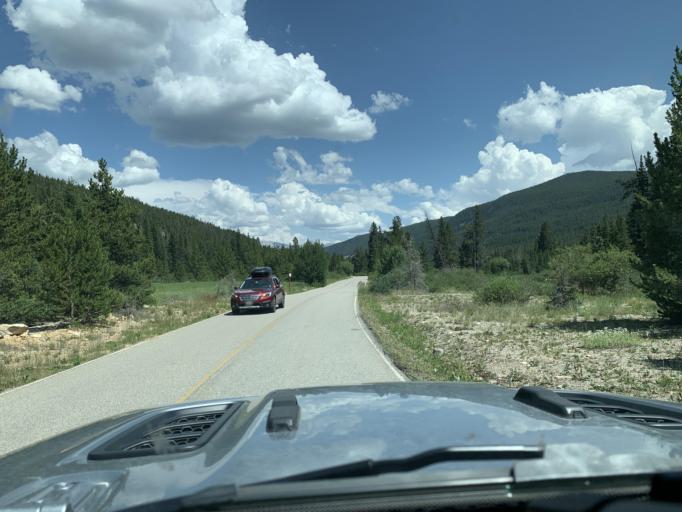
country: US
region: Colorado
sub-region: Lake County
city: Leadville North
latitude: 39.2809
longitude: -106.4399
